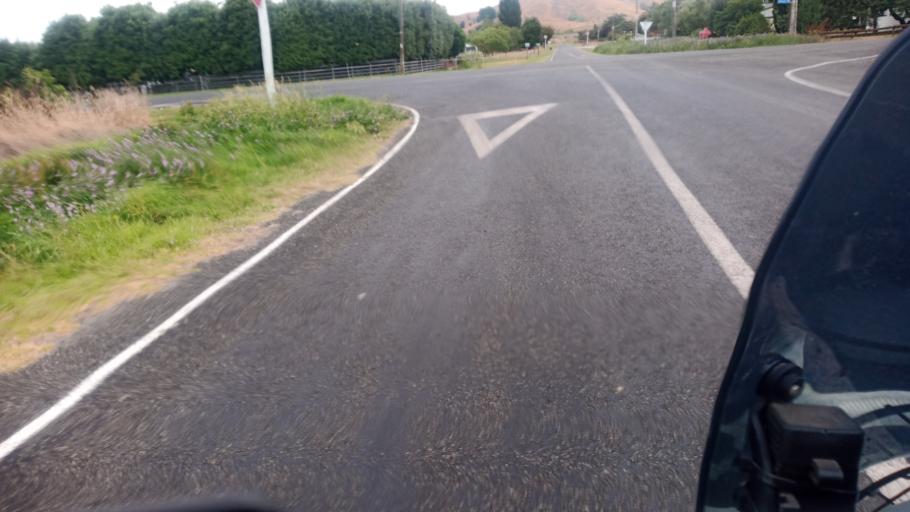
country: NZ
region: Gisborne
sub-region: Gisborne District
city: Gisborne
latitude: -38.6251
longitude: 177.8861
